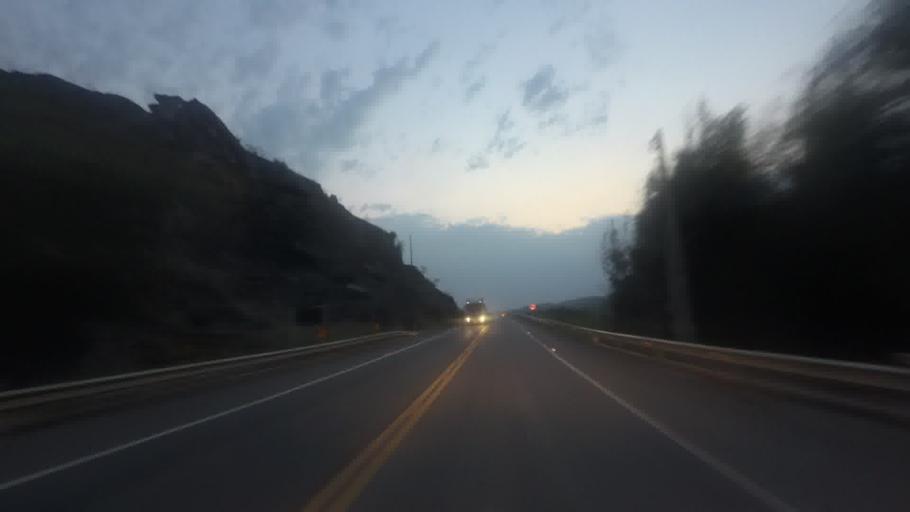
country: BR
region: Minas Gerais
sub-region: Alem Paraiba
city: Alem Paraiba
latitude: -21.9108
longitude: -42.7418
